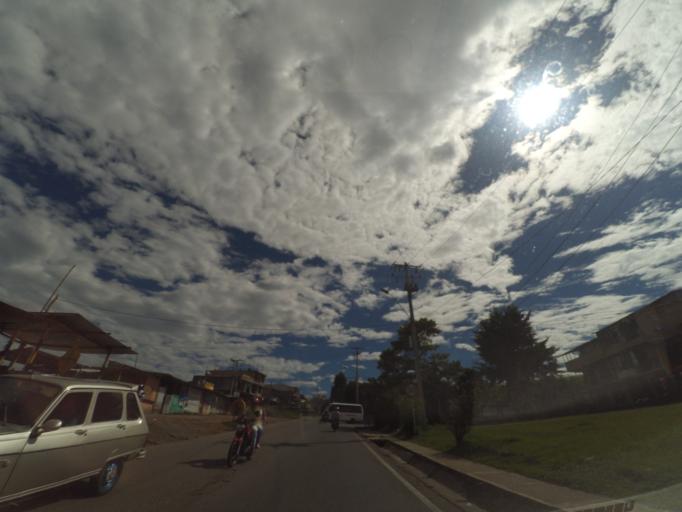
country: CO
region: Cauca
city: Lopez
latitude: 2.4777
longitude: -76.7173
